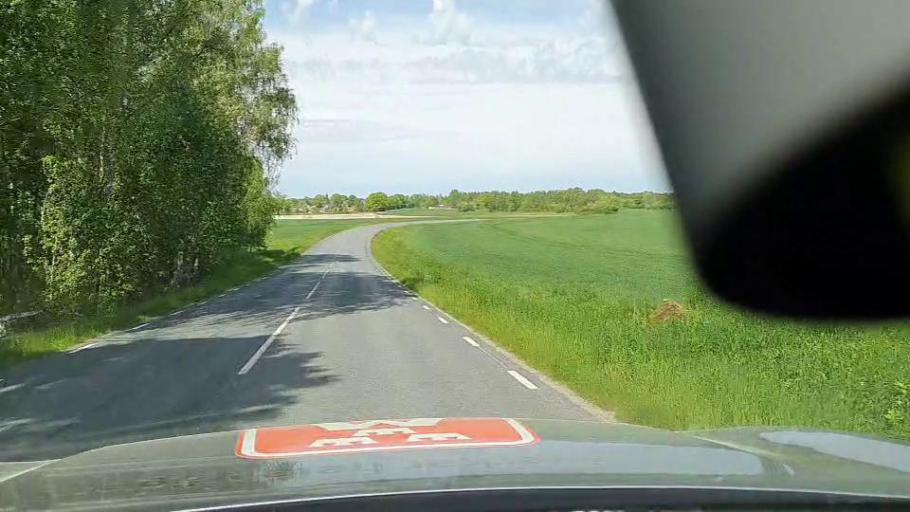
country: SE
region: Soedermanland
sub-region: Eskilstuna Kommun
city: Skogstorp
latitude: 59.3088
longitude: 16.4631
